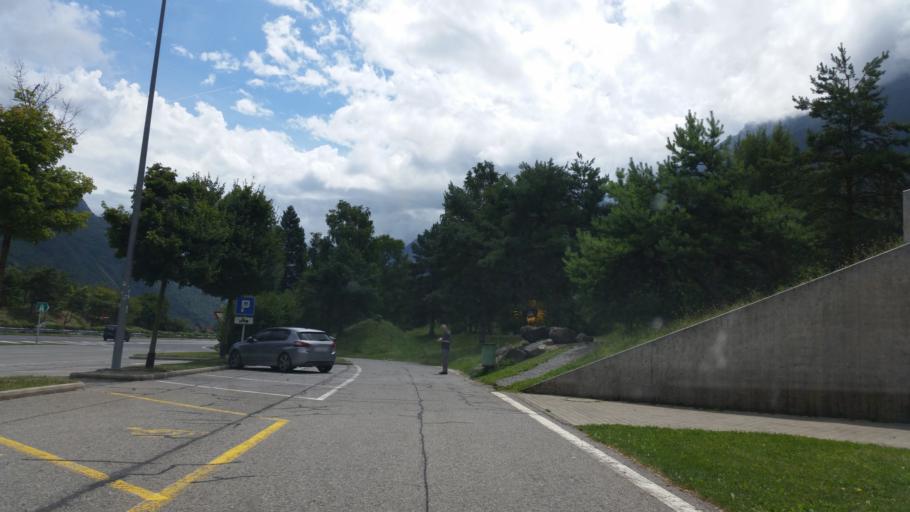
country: CH
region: Valais
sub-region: Martigny District
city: Evionnaz
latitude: 46.1843
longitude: 7.0254
